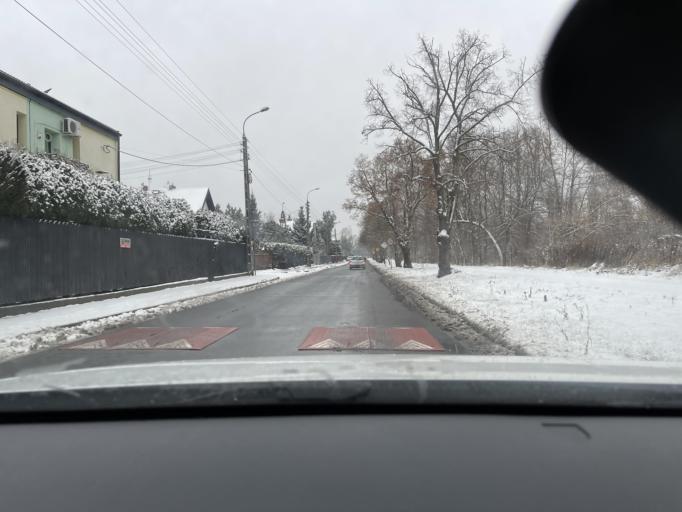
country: PL
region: Masovian Voivodeship
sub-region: Powiat zyrardowski
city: Zyrardow
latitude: 52.0445
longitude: 20.4441
